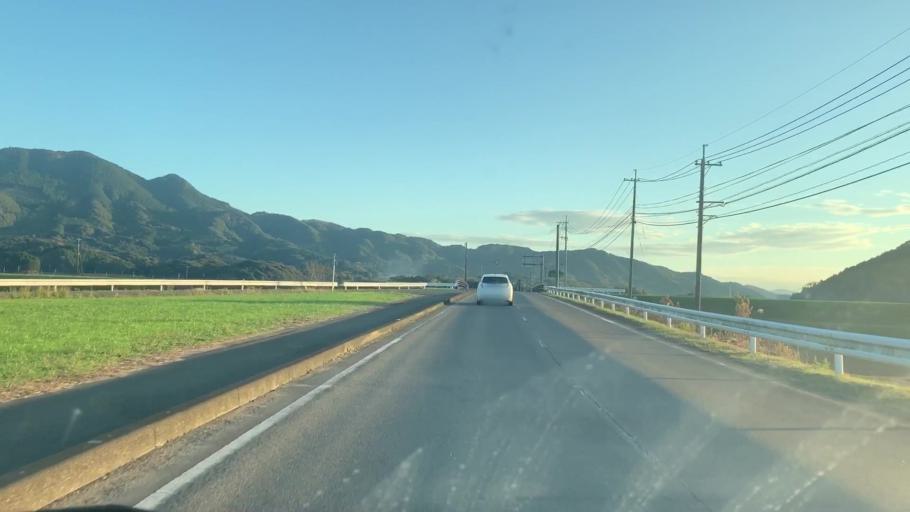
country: JP
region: Saga Prefecture
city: Imaricho-ko
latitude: 33.3003
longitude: 129.9697
